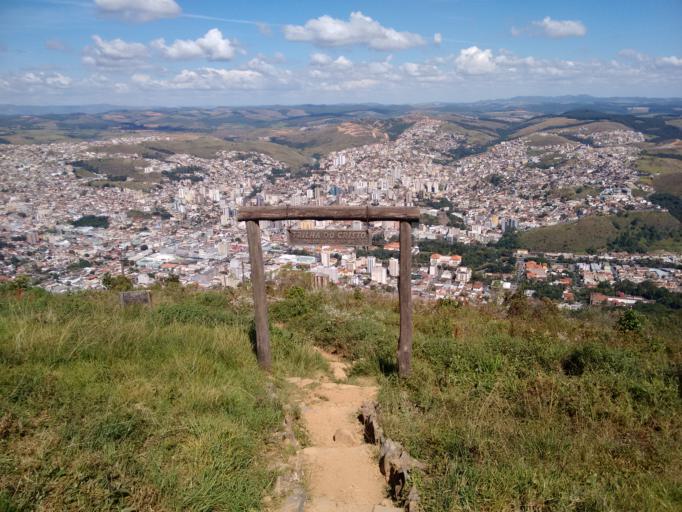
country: BR
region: Minas Gerais
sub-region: Pocos De Caldas
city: Pocos de Caldas
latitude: -21.7732
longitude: -46.5698
